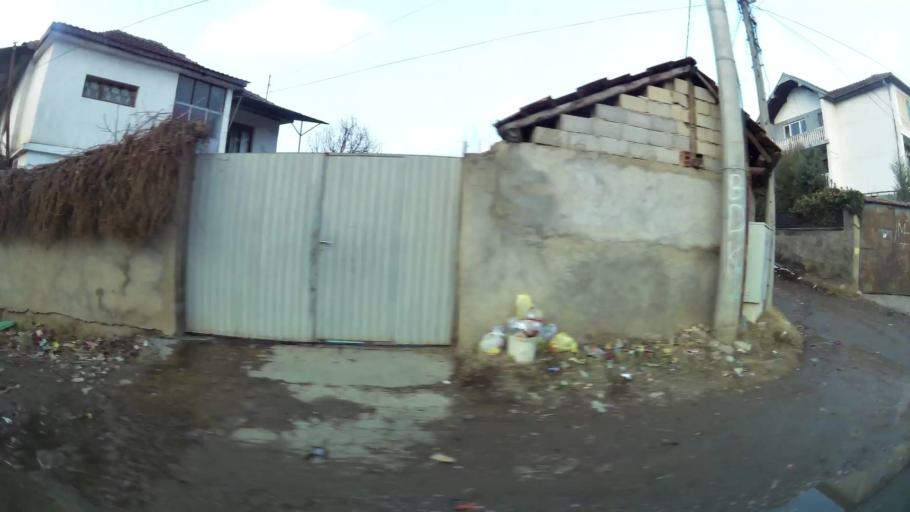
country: MK
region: Aracinovo
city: Arachinovo
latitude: 42.0236
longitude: 21.5586
